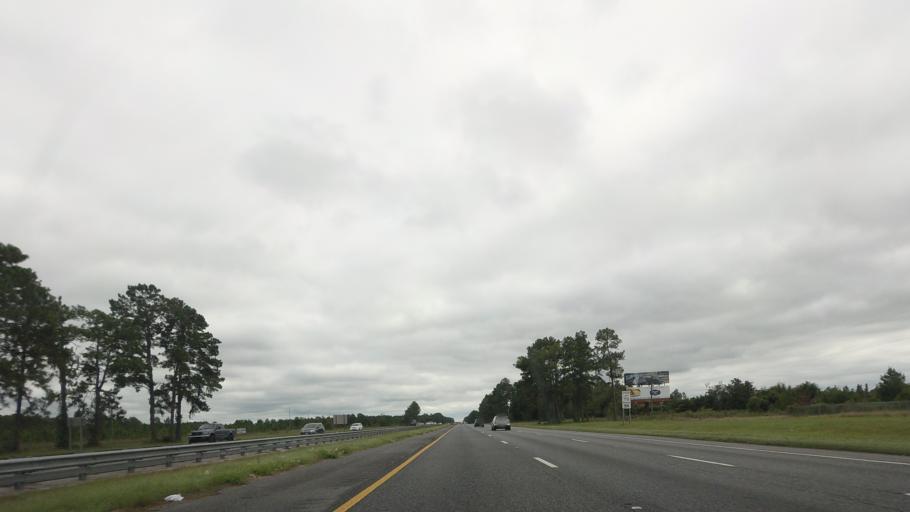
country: US
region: Florida
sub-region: Columbia County
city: Lake City
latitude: 30.1735
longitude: -82.6852
